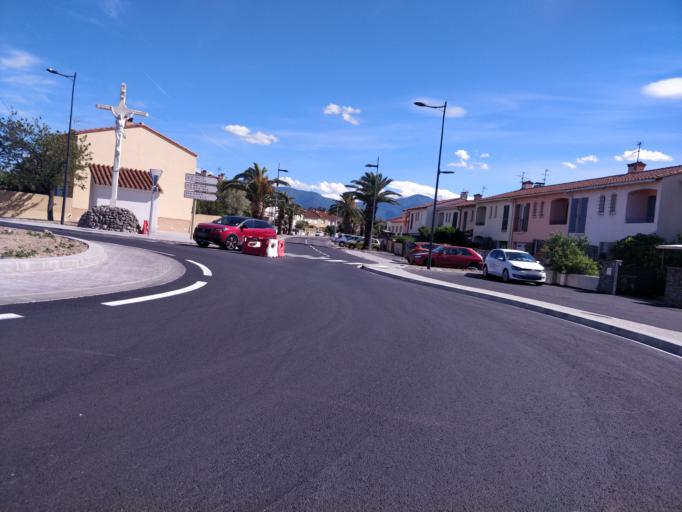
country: FR
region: Languedoc-Roussillon
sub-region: Departement des Pyrenees-Orientales
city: Elne
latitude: 42.6052
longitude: 2.9662
